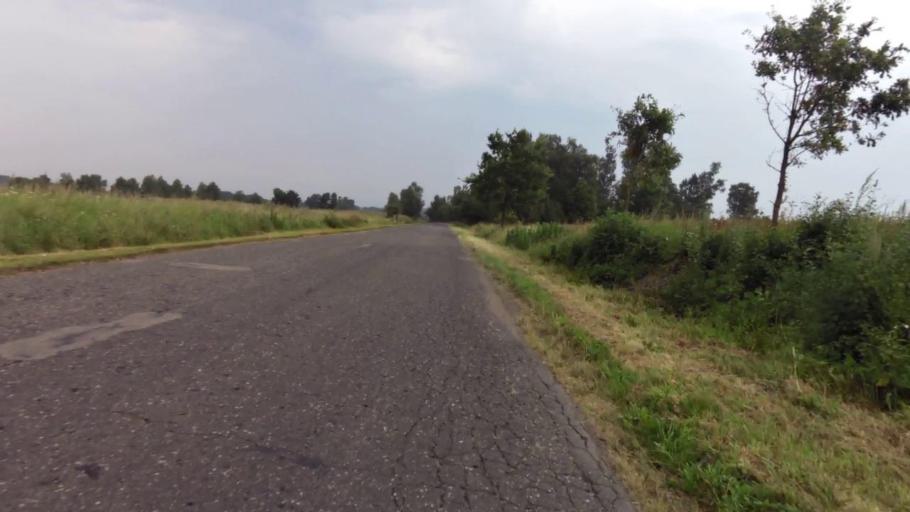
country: PL
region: West Pomeranian Voivodeship
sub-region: Powiat lobeski
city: Wegorzyno
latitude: 53.5012
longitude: 15.6432
